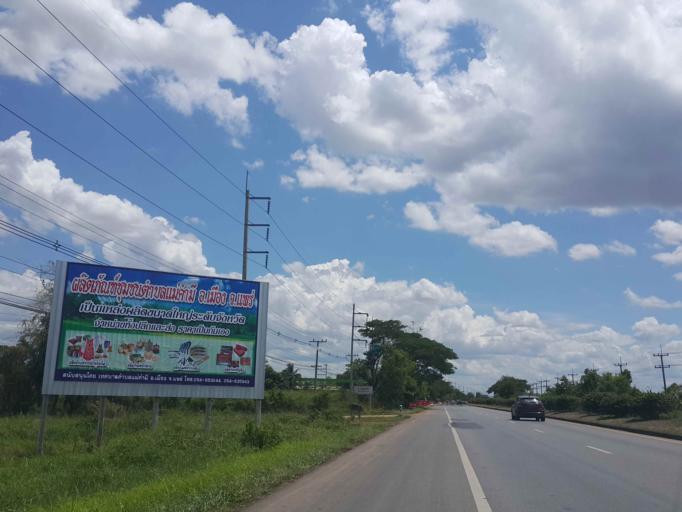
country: TH
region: Phrae
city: Nong Muang Khai
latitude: 18.2541
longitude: 100.2302
